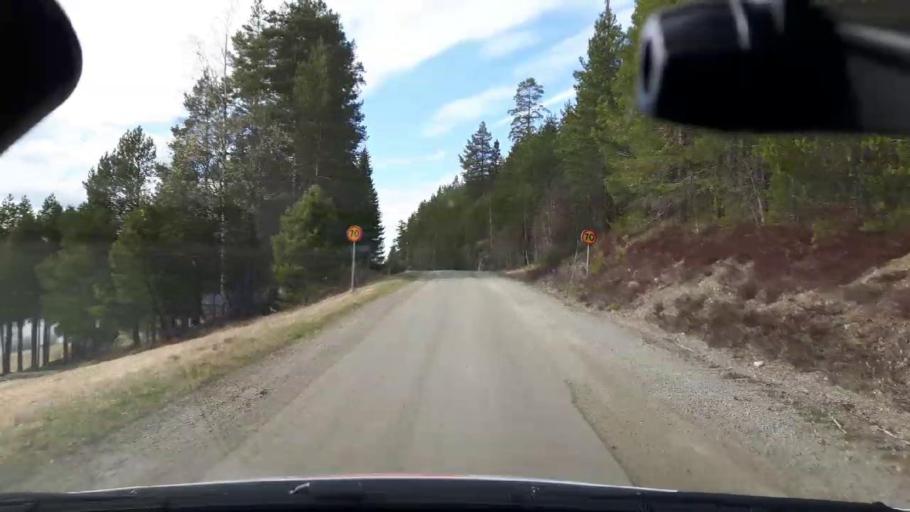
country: SE
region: Jaemtland
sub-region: Bergs Kommun
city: Hoverberg
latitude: 62.7205
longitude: 14.6754
